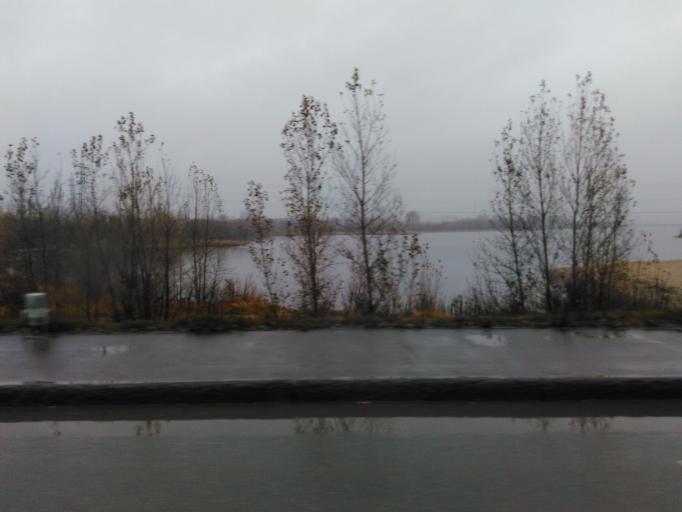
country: RU
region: Tatarstan
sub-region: Gorod Kazan'
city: Kazan
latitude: 55.8000
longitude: 49.0720
